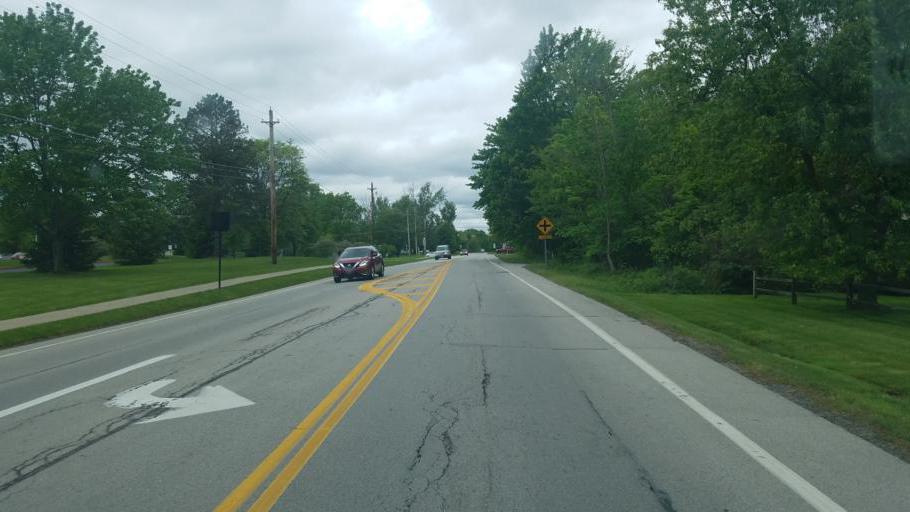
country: US
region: Ohio
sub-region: Summit County
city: Hudson
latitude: 41.2680
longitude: -81.4110
